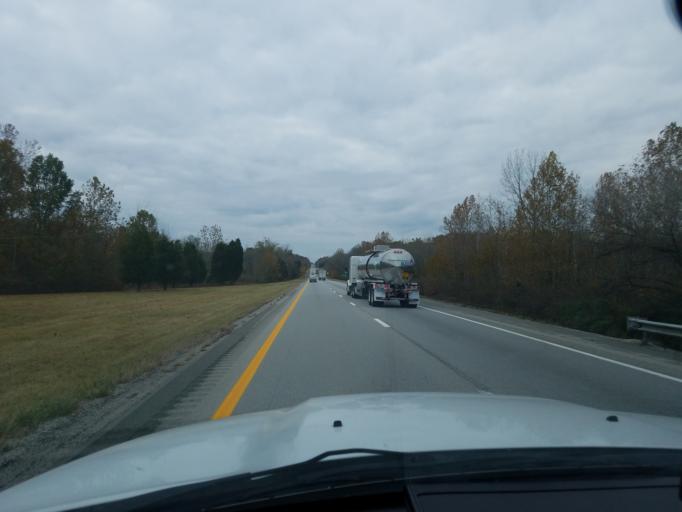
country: US
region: Kentucky
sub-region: Oldham County
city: La Grange
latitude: 38.4257
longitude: -85.3276
